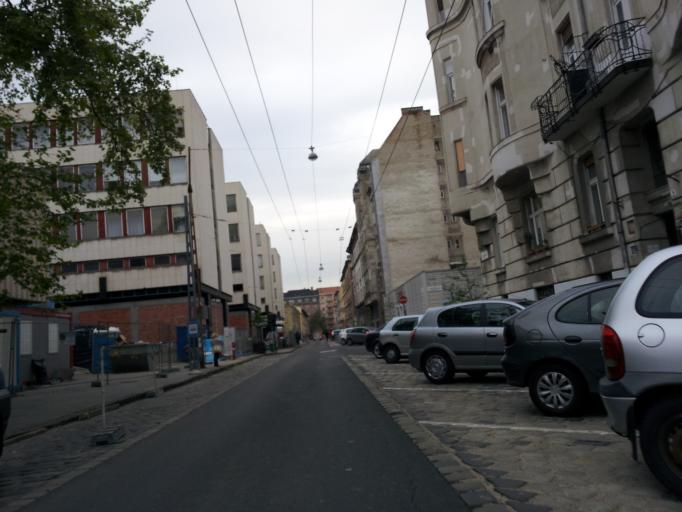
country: HU
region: Budapest
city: Budapest VII. keruelet
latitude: 47.5043
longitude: 19.0788
